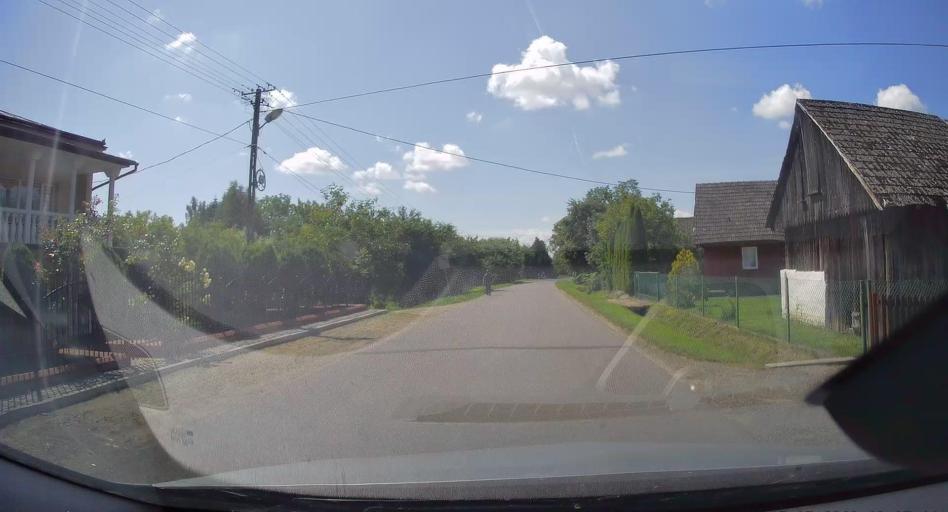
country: PL
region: Subcarpathian Voivodeship
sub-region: Powiat przemyski
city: Medyka
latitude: 49.8209
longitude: 22.8659
